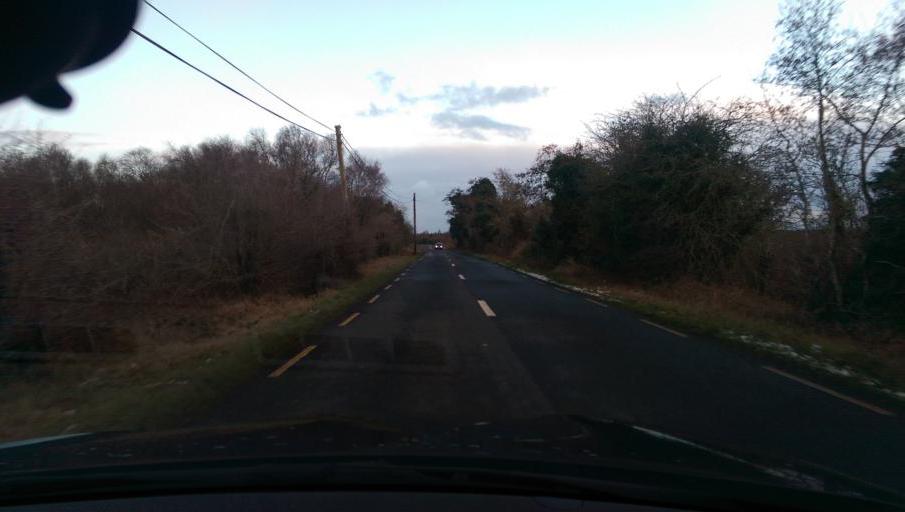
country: IE
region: Connaught
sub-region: County Galway
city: Ballinasloe
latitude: 53.3528
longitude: -8.2546
